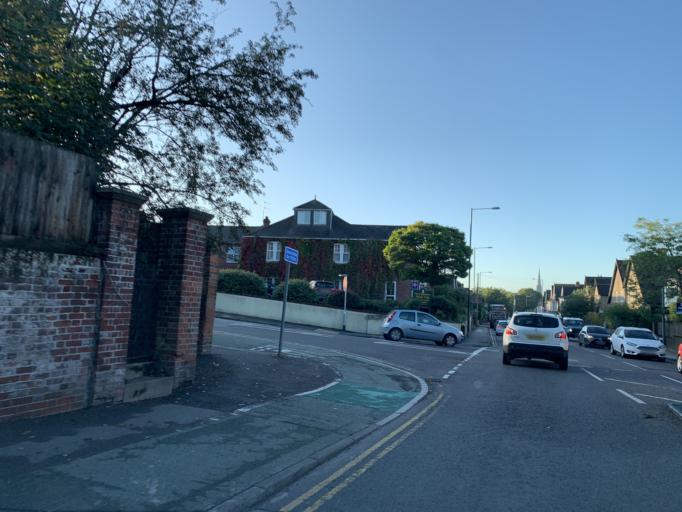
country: GB
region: England
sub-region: Wiltshire
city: Salisbury
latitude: 51.0786
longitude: -1.7972
